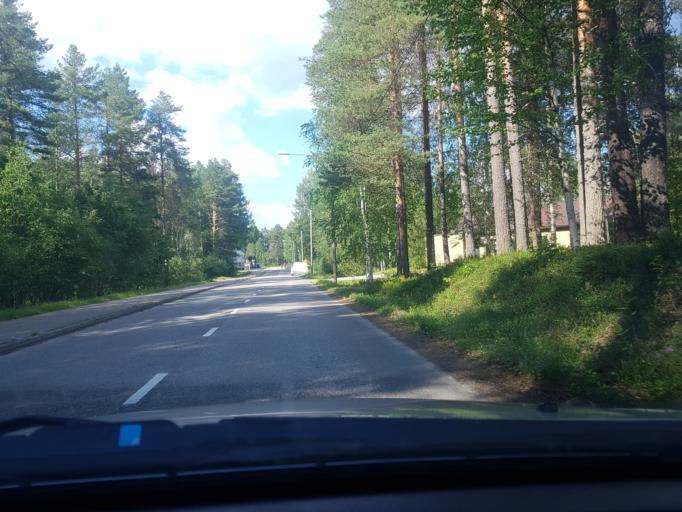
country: FI
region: Kainuu
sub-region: Kehys-Kainuu
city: Kuhmo
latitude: 64.1316
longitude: 29.5443
